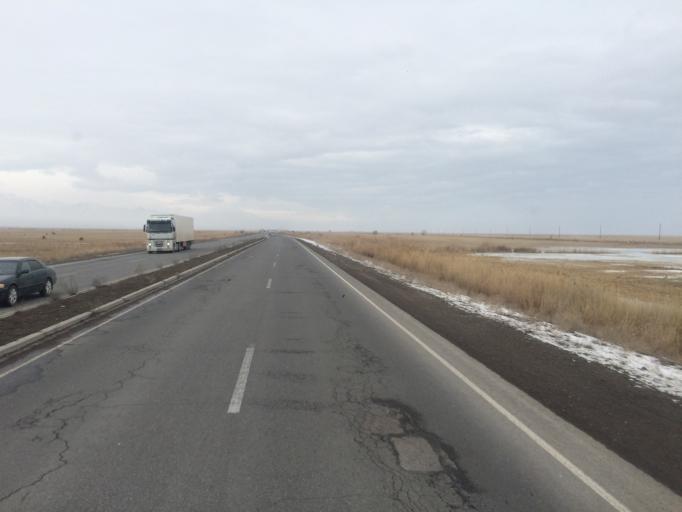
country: KG
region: Chuy
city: Tokmok
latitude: 43.3512
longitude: 75.4684
